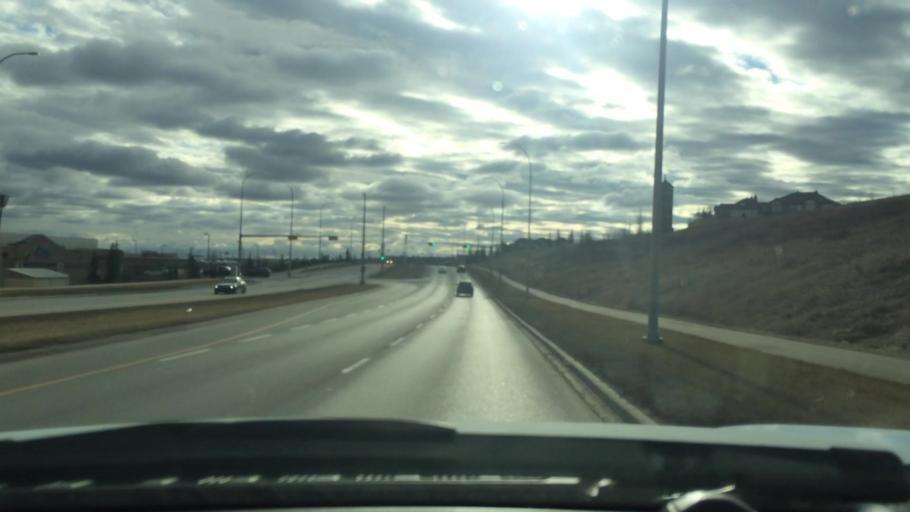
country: CA
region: Alberta
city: Calgary
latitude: 51.1641
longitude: -114.1289
